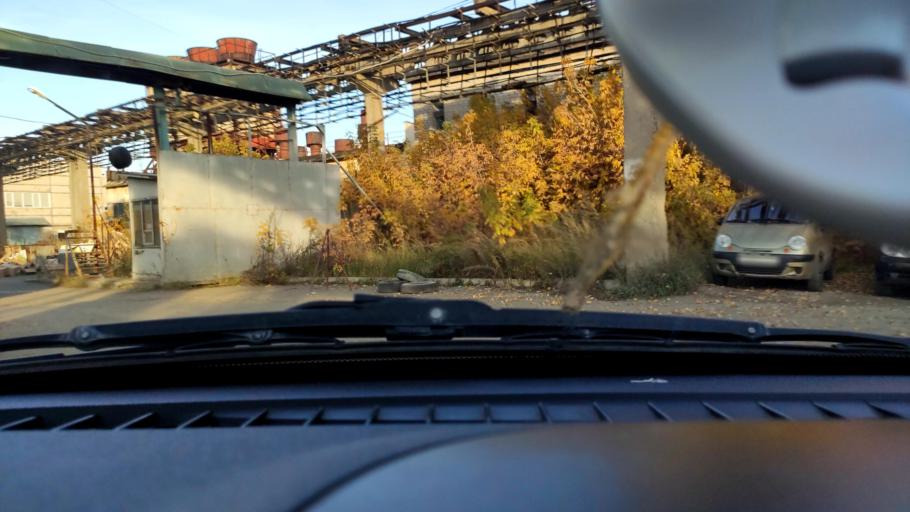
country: RU
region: Perm
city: Kondratovo
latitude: 58.0104
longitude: 56.1660
